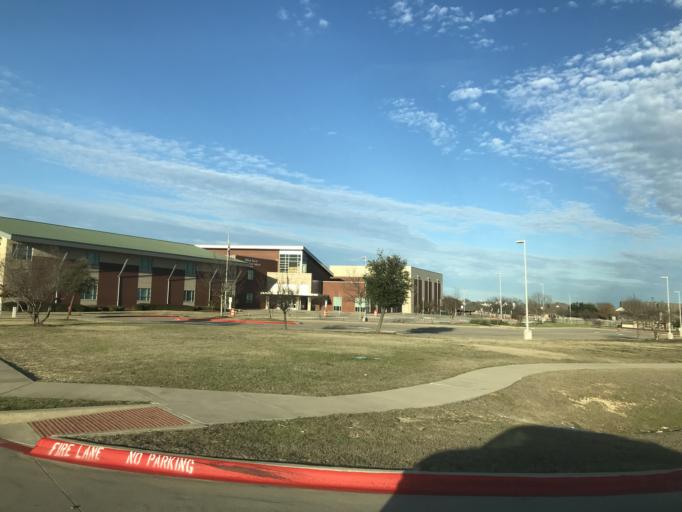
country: US
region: Texas
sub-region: Tarrant County
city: Saginaw
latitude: 32.8586
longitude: -97.3878
